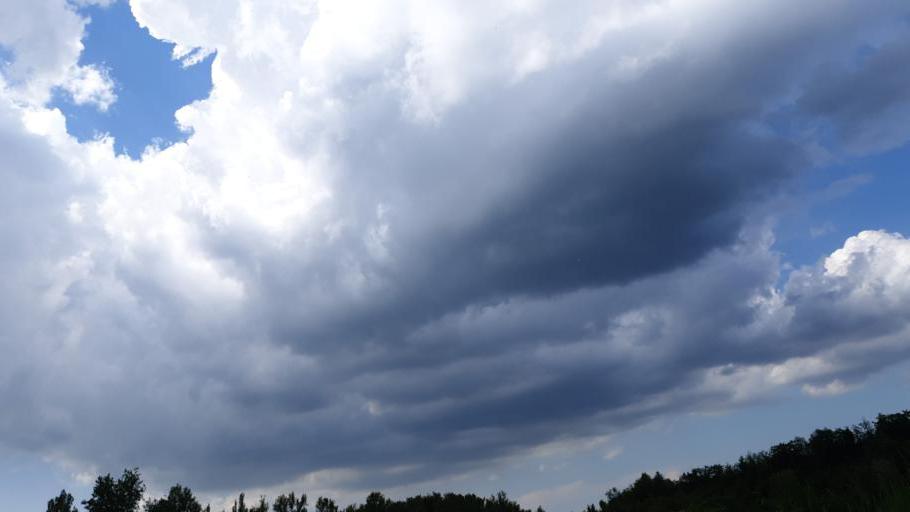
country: IT
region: Emilia-Romagna
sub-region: Provincia di Bologna
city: Borgonuovo
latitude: 44.4267
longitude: 11.2865
